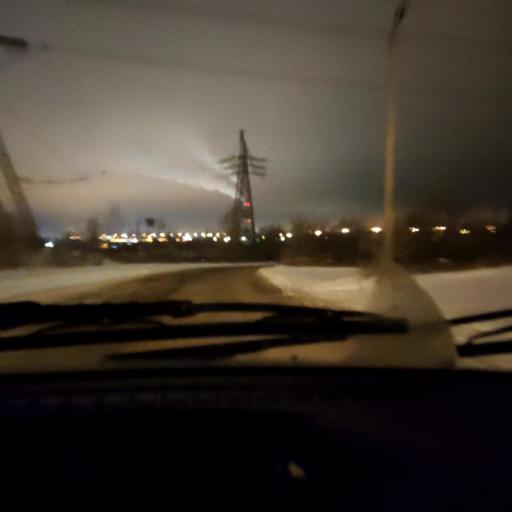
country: RU
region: Samara
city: Zhigulevsk
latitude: 53.4836
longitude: 49.5064
